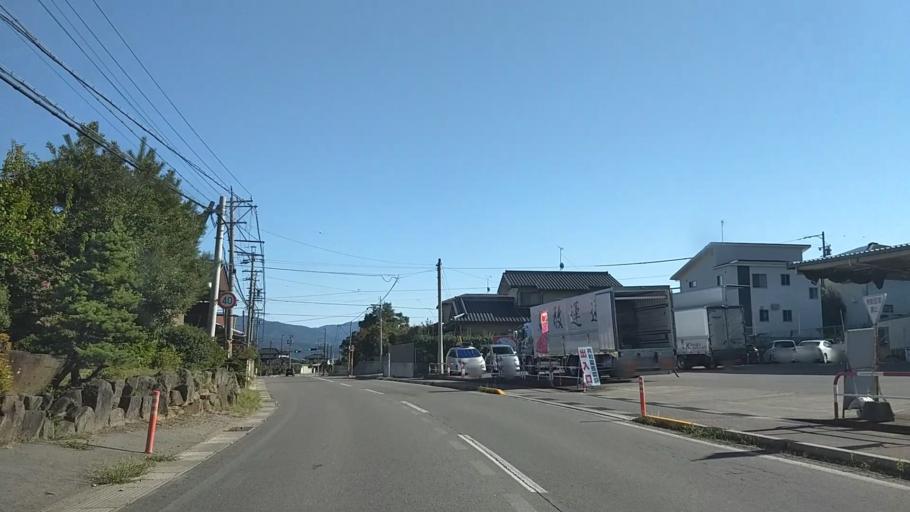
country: JP
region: Nagano
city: Nagano-shi
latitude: 36.5984
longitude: 138.1313
